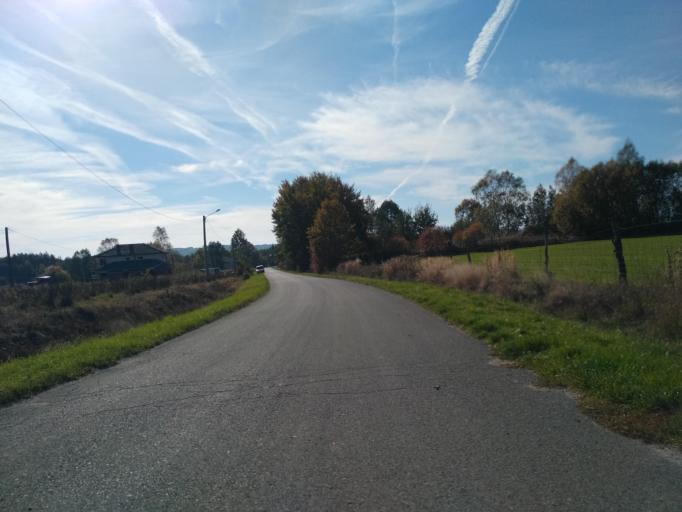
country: PL
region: Subcarpathian Voivodeship
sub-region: Powiat rzeszowski
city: Trzciana
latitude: 50.0871
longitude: 21.8137
